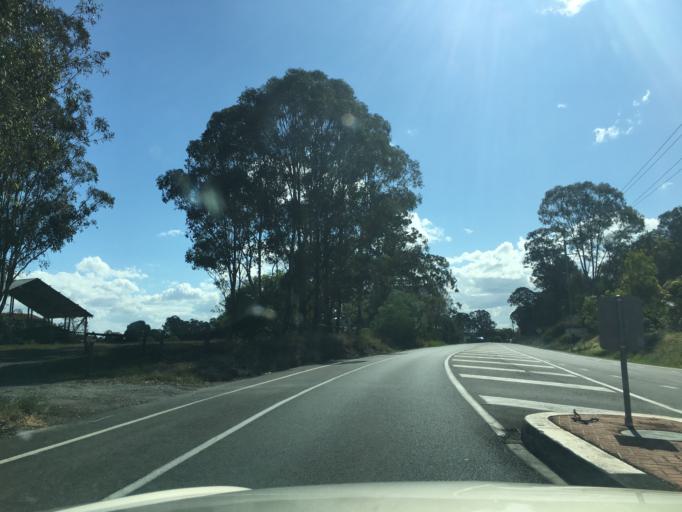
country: AU
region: Queensland
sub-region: Logan
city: Waterford West
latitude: -27.7093
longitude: 153.1440
